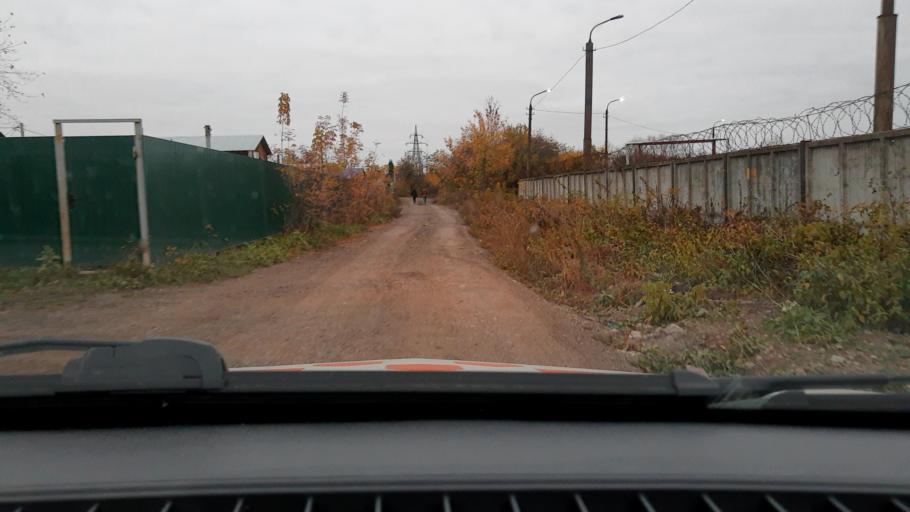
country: RU
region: Bashkortostan
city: Ufa
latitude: 54.8270
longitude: 56.1006
